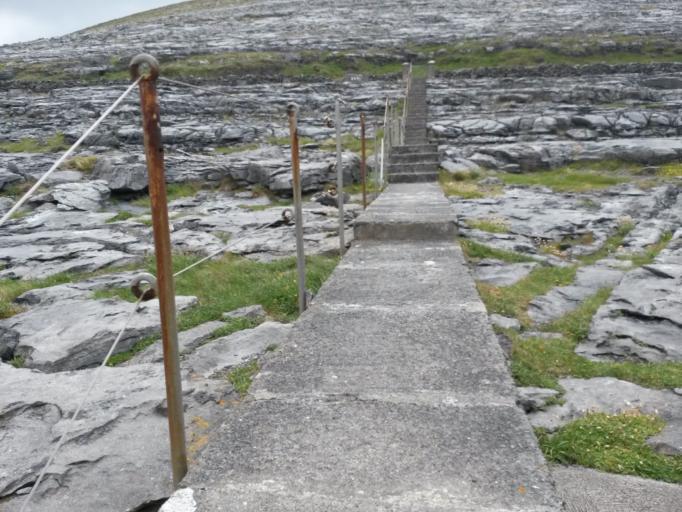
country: IE
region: Connaught
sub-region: County Galway
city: Bearna
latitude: 53.1539
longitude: -9.2650
